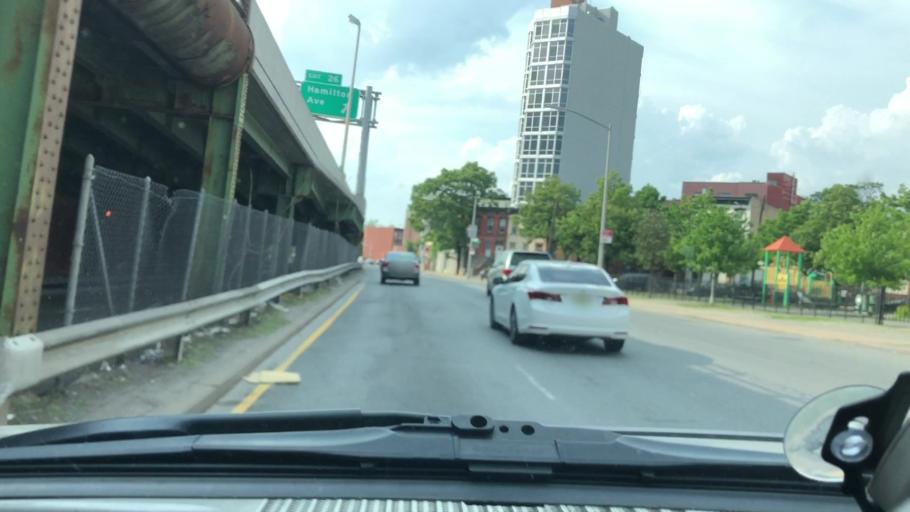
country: US
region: New York
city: New York City
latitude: 40.6764
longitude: -74.0011
